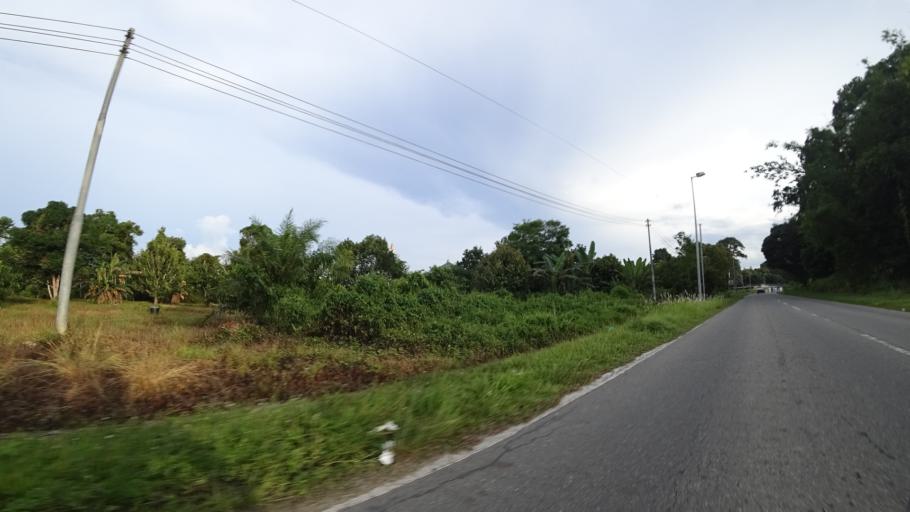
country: BN
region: Brunei and Muara
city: Bandar Seri Begawan
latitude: 4.8522
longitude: 114.8221
